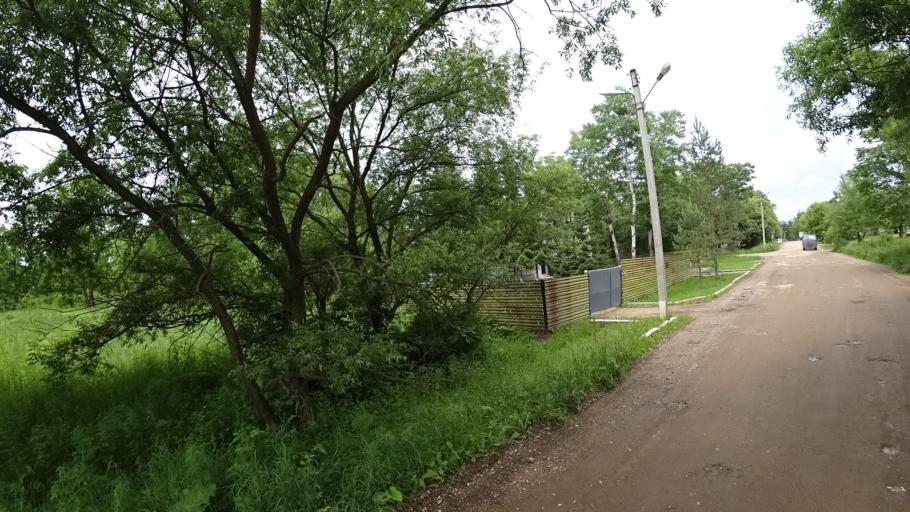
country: RU
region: Primorskiy
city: Novosysoyevka
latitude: 44.2264
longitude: 133.3618
